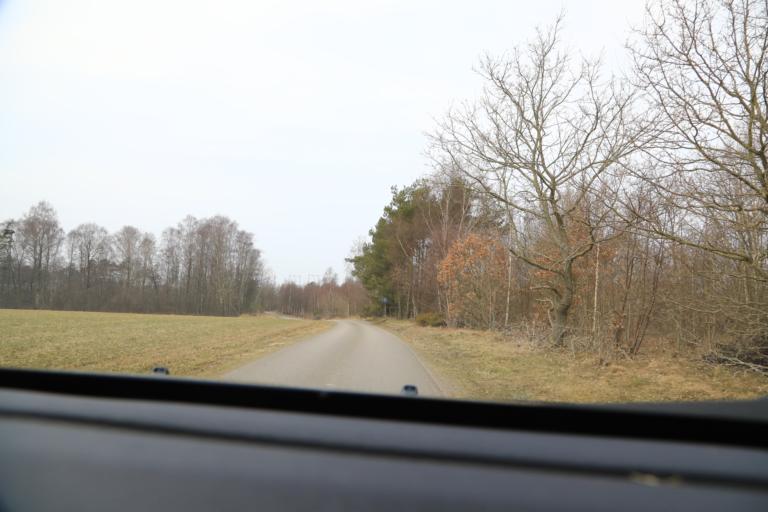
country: SE
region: Halland
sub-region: Kungsbacka Kommun
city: Frillesas
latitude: 57.2656
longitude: 12.1368
